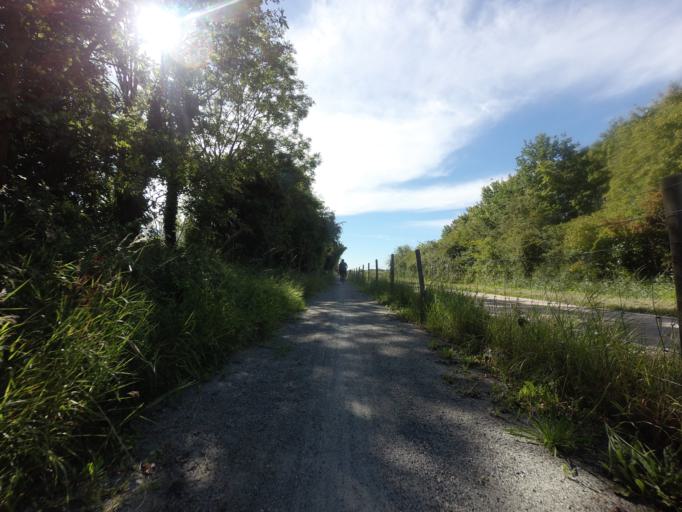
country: GB
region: England
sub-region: Kent
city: Birchington-on-Sea
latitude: 51.3624
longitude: 1.2189
